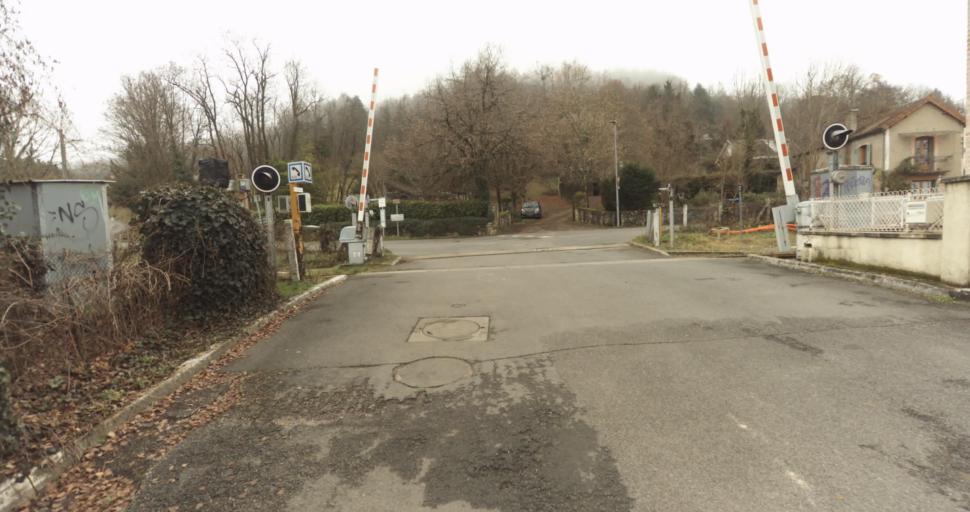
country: FR
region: Midi-Pyrenees
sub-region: Departement du Lot
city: Figeac
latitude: 44.6058
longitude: 2.0392
